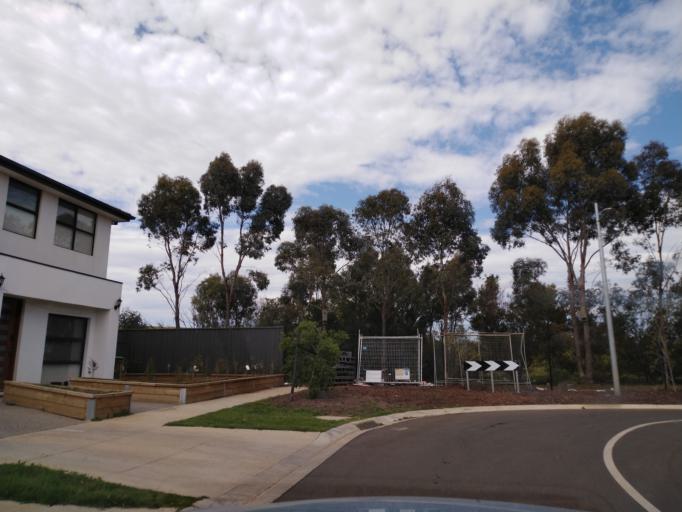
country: AU
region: Victoria
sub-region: Wyndham
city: Williams Landing
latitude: -37.8496
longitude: 144.7166
